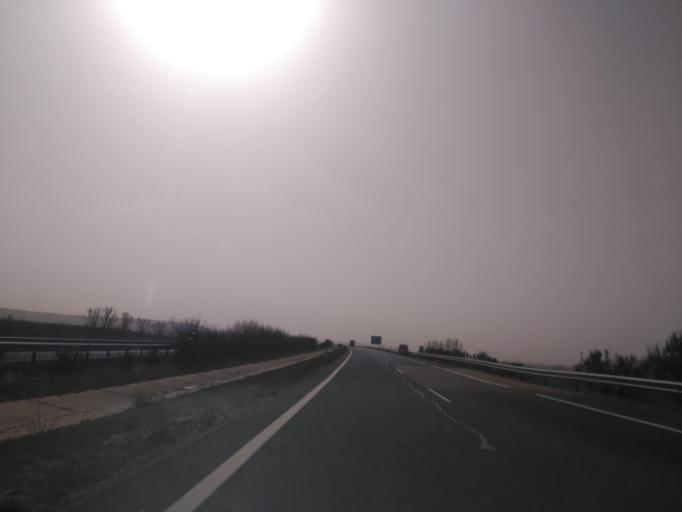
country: ES
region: Castille and Leon
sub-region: Provincia de Palencia
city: Pina de Campos
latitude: 42.2060
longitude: -4.4485
